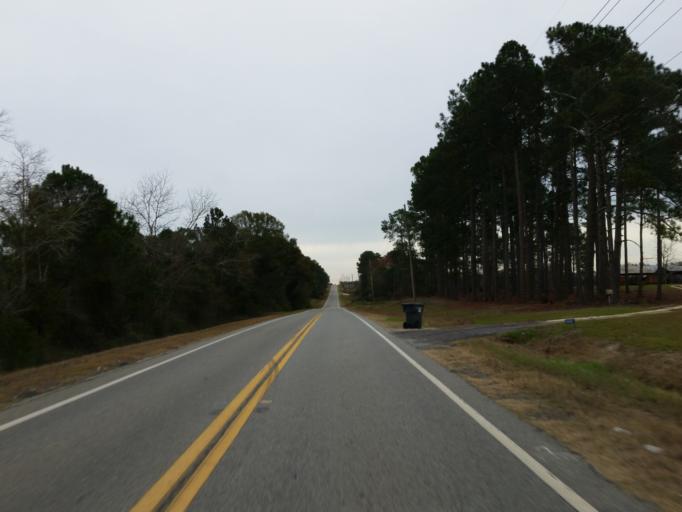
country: US
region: Georgia
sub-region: Crisp County
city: Cordele
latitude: 31.9202
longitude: -83.7155
